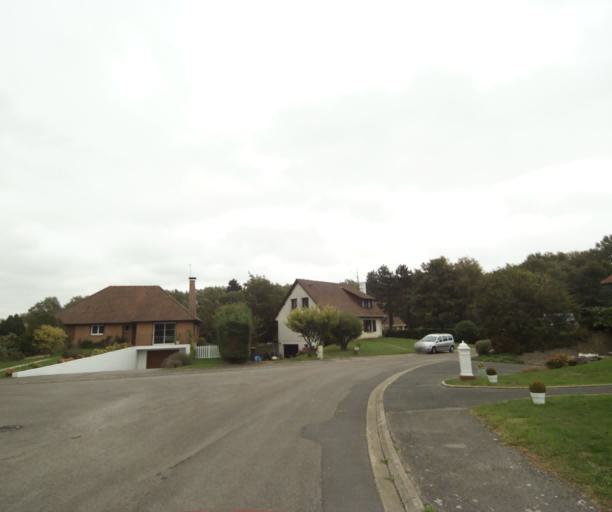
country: FR
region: Nord-Pas-de-Calais
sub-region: Departement du Pas-de-Calais
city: Etaples
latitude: 50.5278
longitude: 1.6401
